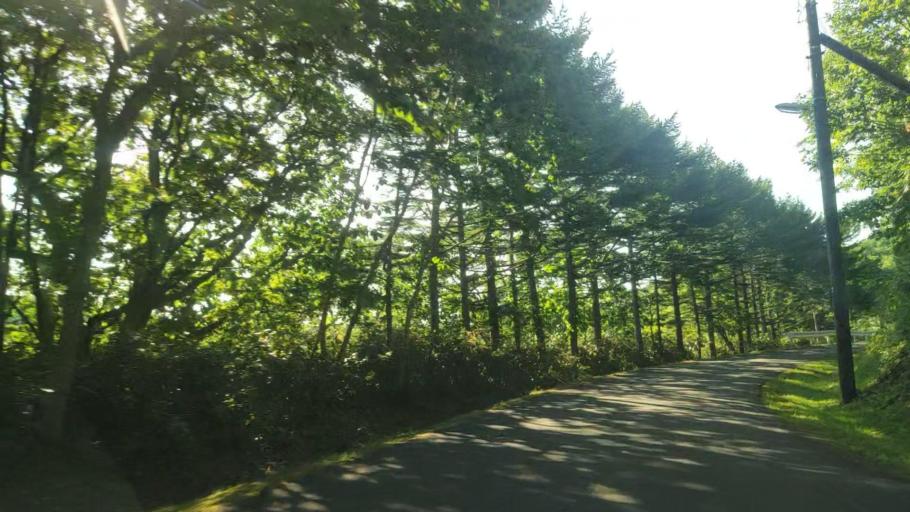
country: JP
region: Hokkaido
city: Wakkanai
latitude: 45.4140
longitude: 141.6685
